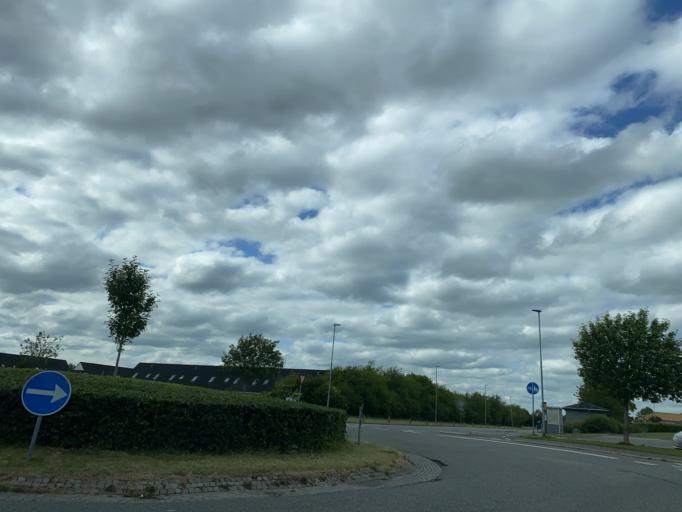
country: DK
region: Central Jutland
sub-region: Arhus Kommune
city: Framlev
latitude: 56.1437
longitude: 9.9878
